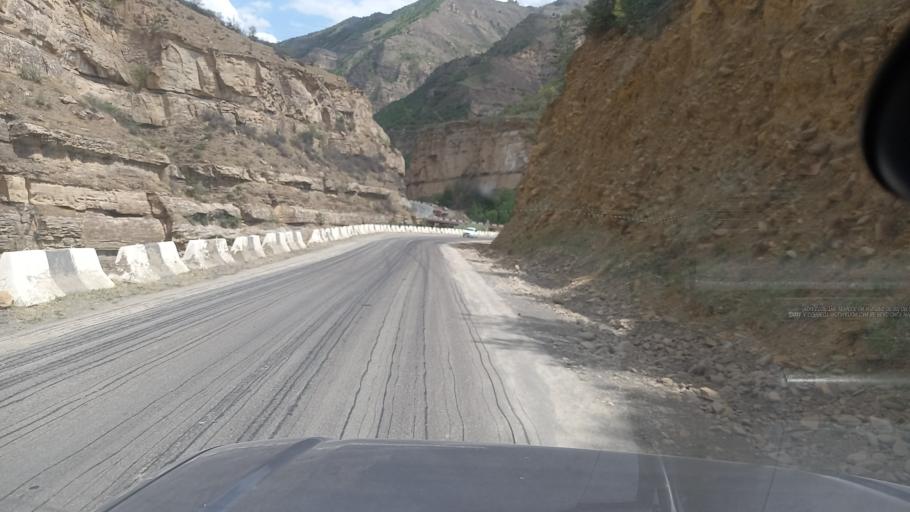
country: RU
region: Dagestan
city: Gunib
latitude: 42.3198
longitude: 46.9280
